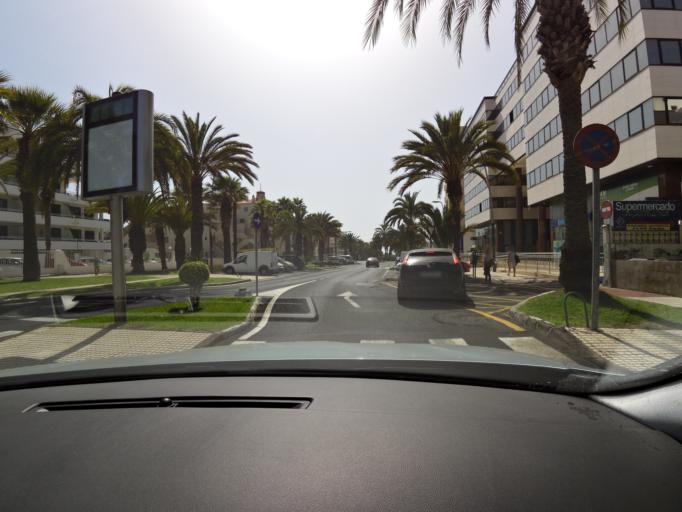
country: ES
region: Canary Islands
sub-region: Provincia de Santa Cruz de Tenerife
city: Playa de las Americas
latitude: 28.0569
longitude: -16.7284
